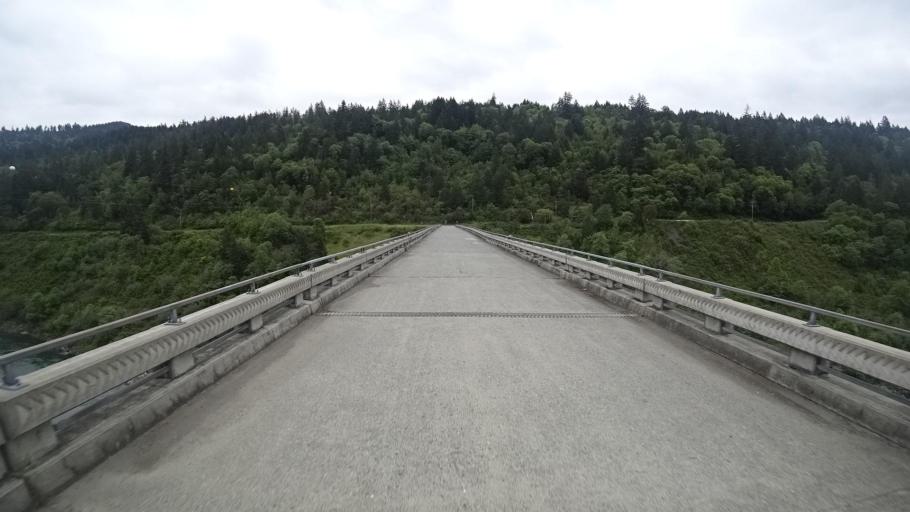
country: US
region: California
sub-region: Humboldt County
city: Willow Creek
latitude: 41.2079
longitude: -123.7570
